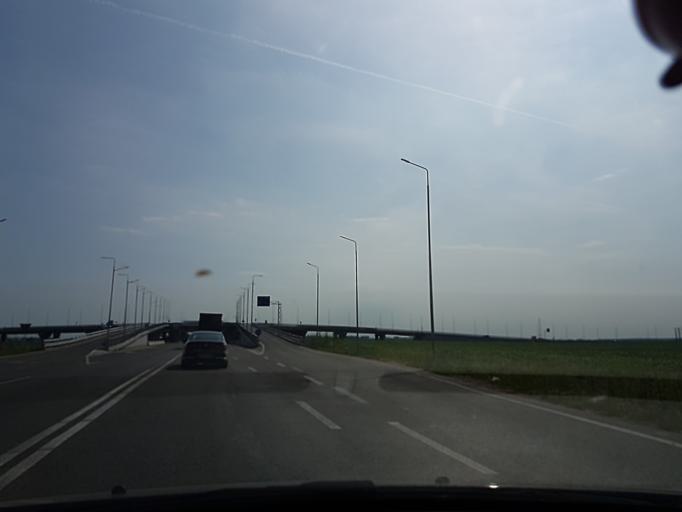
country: RO
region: Prahova
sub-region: Comuna Blejoiu
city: Ploiestiori
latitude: 44.9792
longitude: 25.9948
